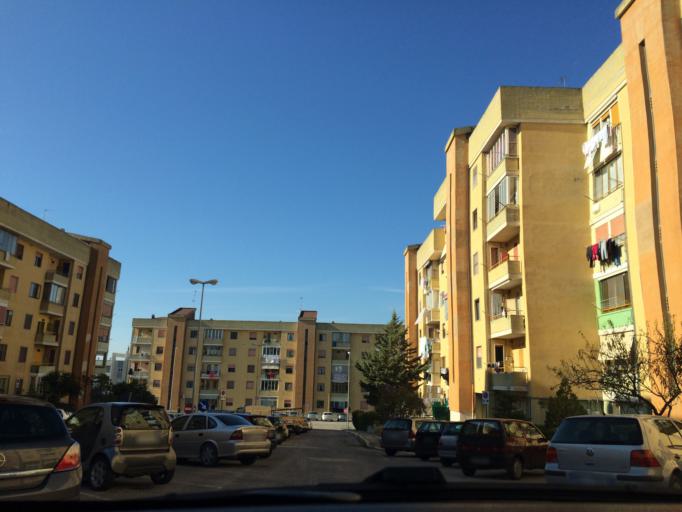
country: IT
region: Basilicate
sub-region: Provincia di Matera
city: Matera
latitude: 40.6804
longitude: 16.5770
